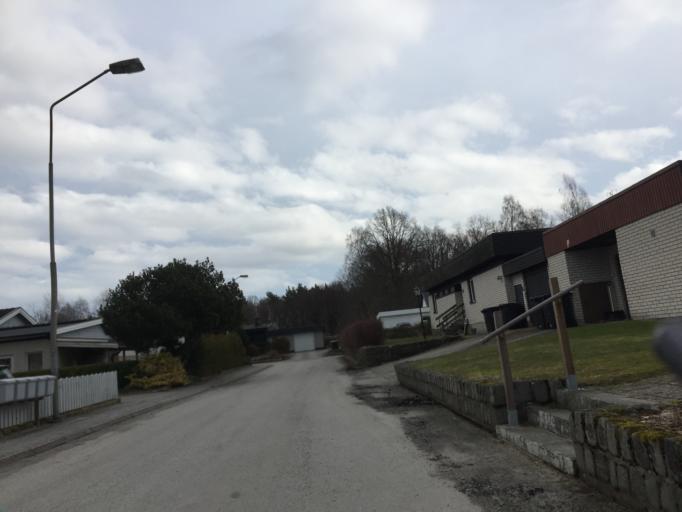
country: SE
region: Blekinge
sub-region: Karlshamns Kommun
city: Morrum
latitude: 56.1879
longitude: 14.7583
